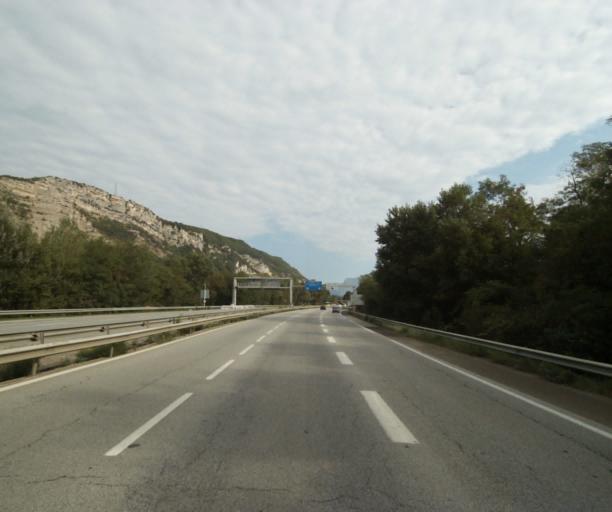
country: FR
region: Rhone-Alpes
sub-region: Departement de l'Isere
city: Le Pont-de-Claix
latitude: 45.1314
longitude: 5.6903
